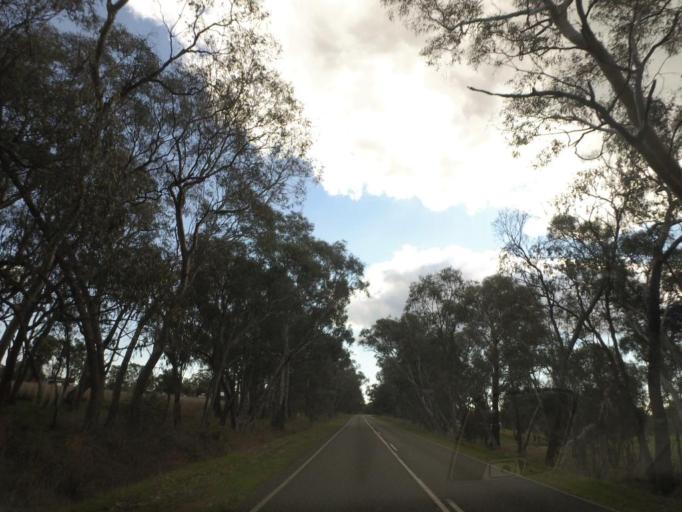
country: AU
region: New South Wales
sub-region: Corowa Shire
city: Howlong
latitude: -36.1859
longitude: 146.6096
